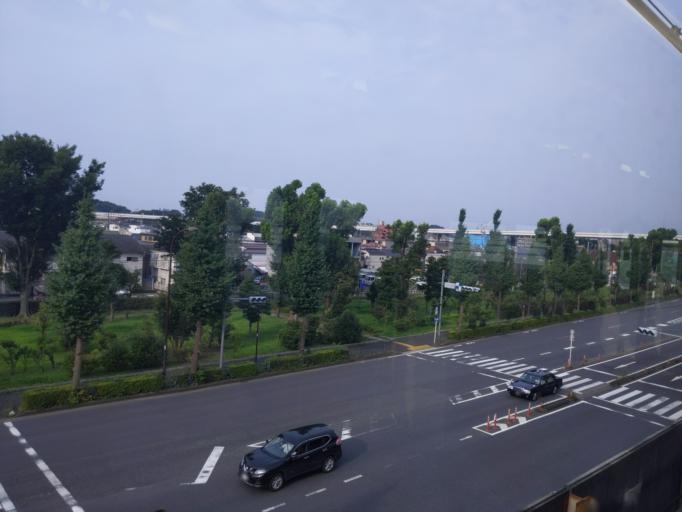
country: JP
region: Saitama
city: Wako
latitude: 35.7915
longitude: 139.6476
